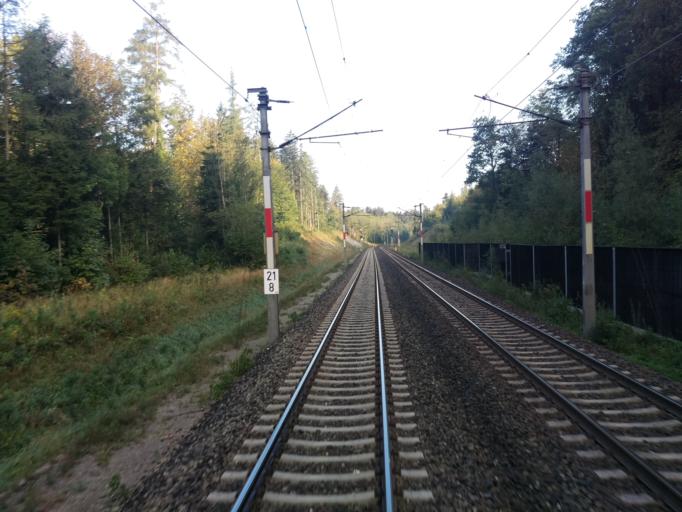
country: AT
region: Salzburg
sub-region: Politischer Bezirk Hallein
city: Adnet
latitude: 47.6565
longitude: 13.1255
